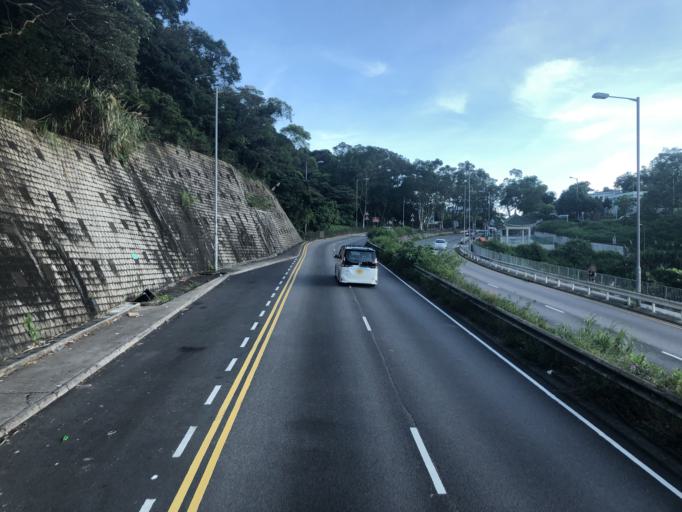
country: HK
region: Sai Kung
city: Sai Kung
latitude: 22.3417
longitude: 114.2485
